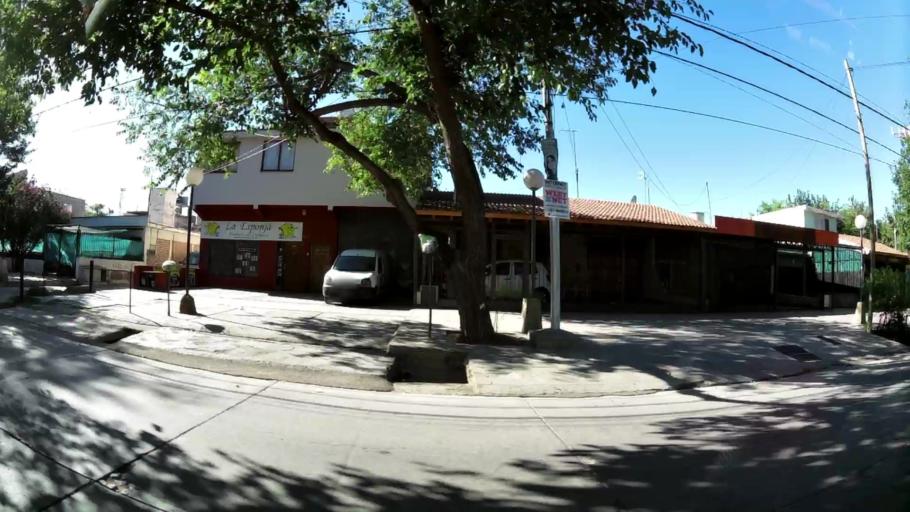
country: AR
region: Mendoza
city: Las Heras
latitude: -32.8419
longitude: -68.8311
